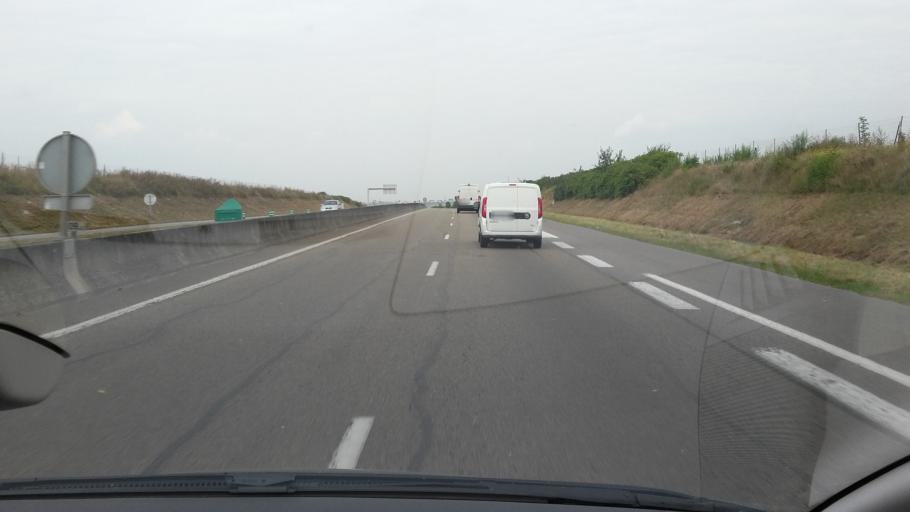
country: FR
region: Champagne-Ardenne
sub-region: Departement de la Marne
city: Cernay-les-Reims
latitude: 49.2439
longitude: 4.0806
